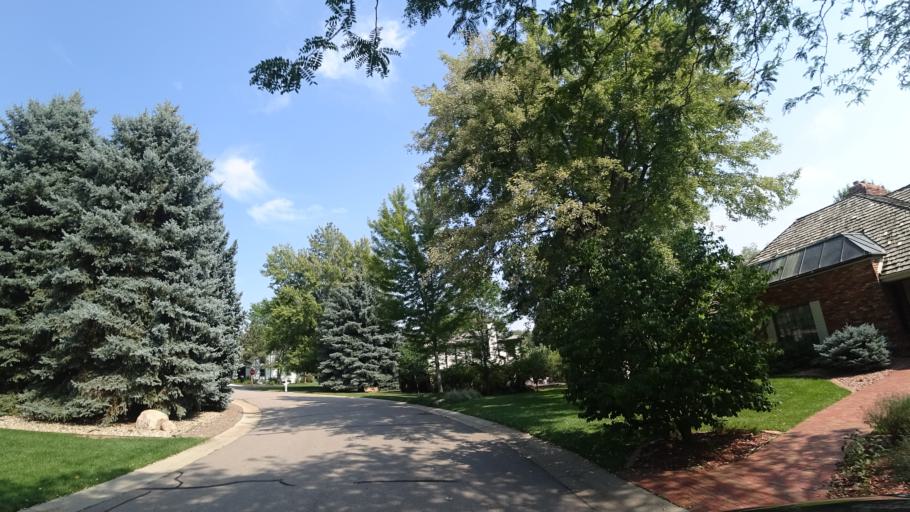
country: US
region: Colorado
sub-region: Arapahoe County
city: Greenwood Village
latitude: 39.6118
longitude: -104.9654
